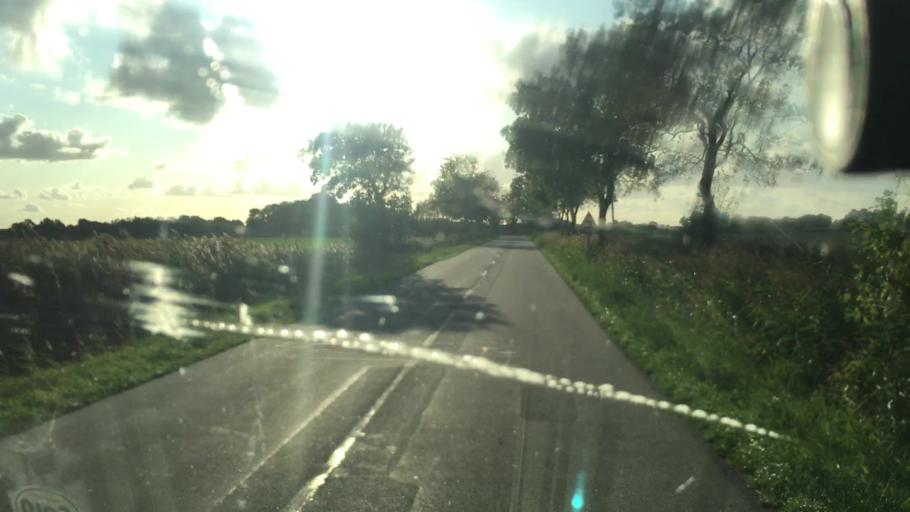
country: DE
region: Lower Saxony
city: Werdum
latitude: 53.6630
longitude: 7.7458
